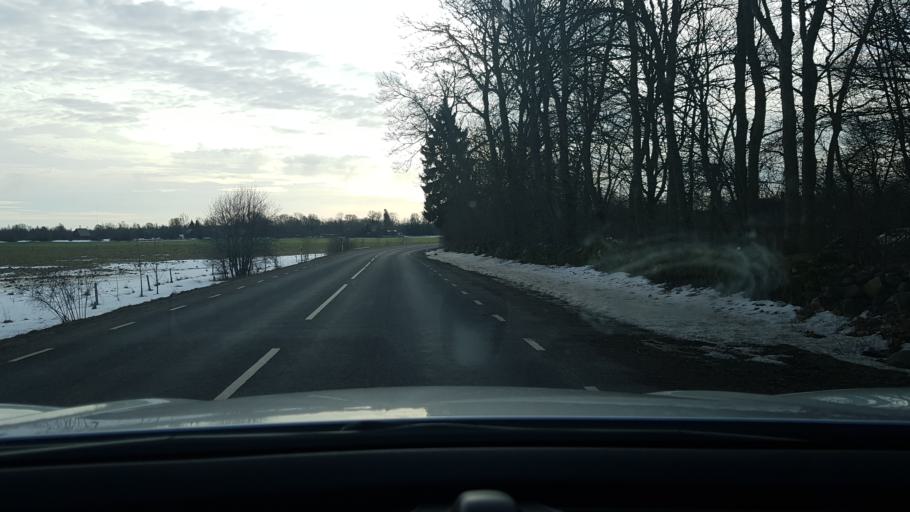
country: EE
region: Saare
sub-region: Kuressaare linn
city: Kuressaare
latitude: 58.2965
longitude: 22.5415
